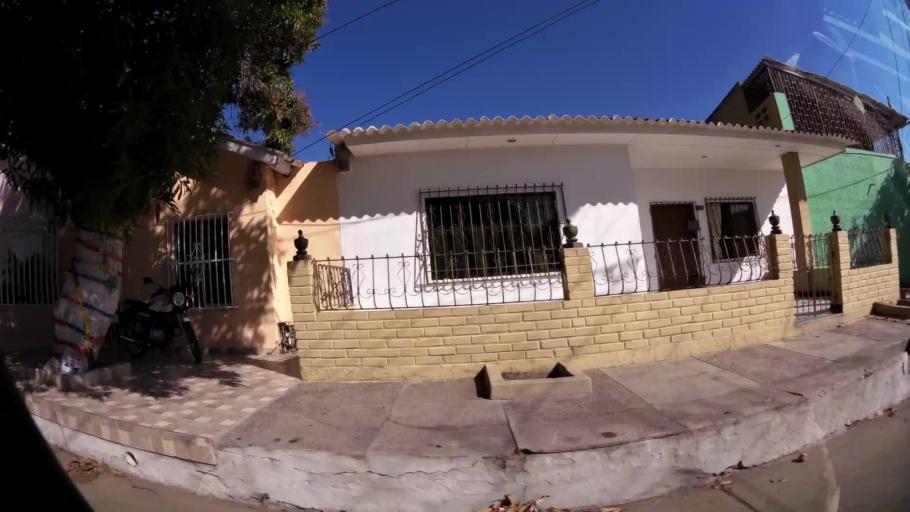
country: CO
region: Atlantico
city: Barranquilla
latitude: 10.9682
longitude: -74.7845
